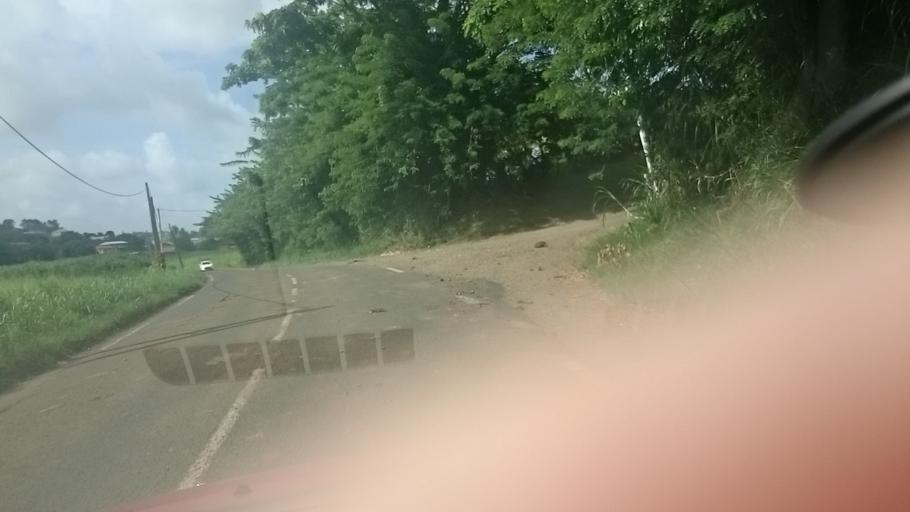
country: MQ
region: Martinique
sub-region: Martinique
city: Saint-Esprit
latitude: 14.5764
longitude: -60.9293
